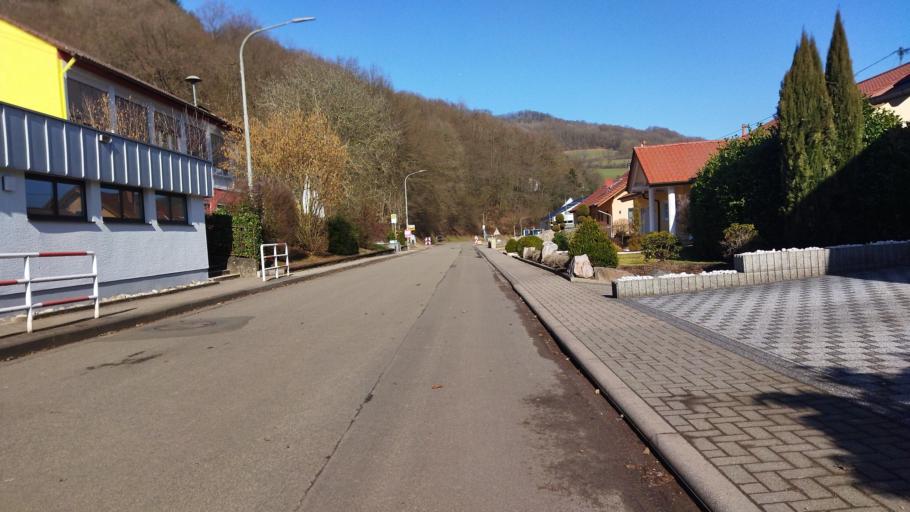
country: DE
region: Rheinland-Pfalz
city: Etschberg
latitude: 49.5138
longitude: 7.4430
